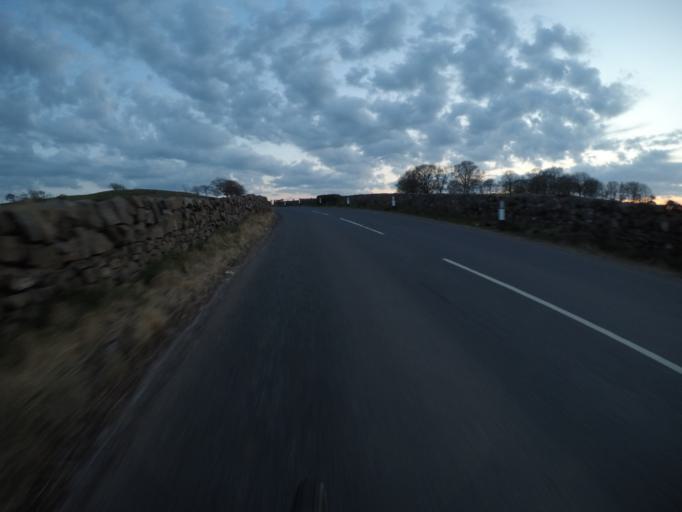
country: GB
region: Scotland
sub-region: South Ayrshire
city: Dundonald
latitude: 55.5624
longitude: -4.6060
